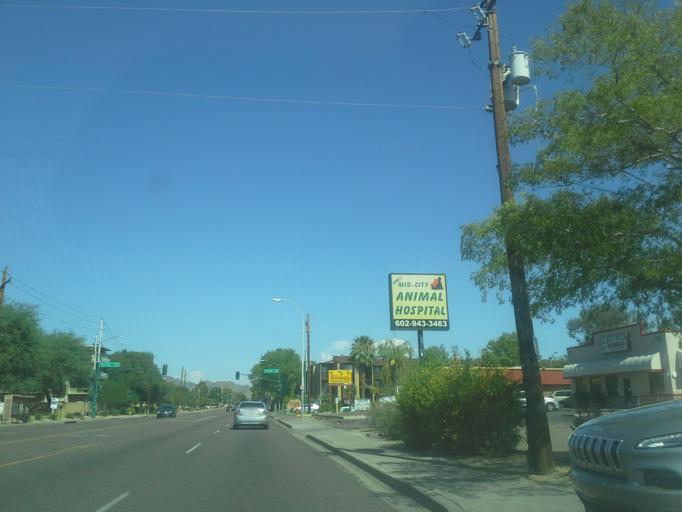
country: US
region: Arizona
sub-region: Maricopa County
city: Glendale
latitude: 33.5385
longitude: -112.0975
